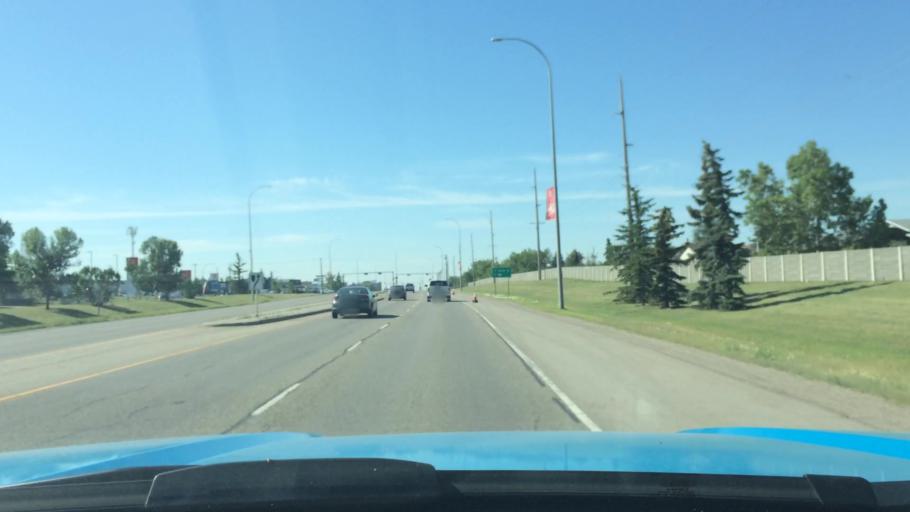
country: CA
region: Alberta
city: Calgary
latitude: 51.0614
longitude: -114.0018
